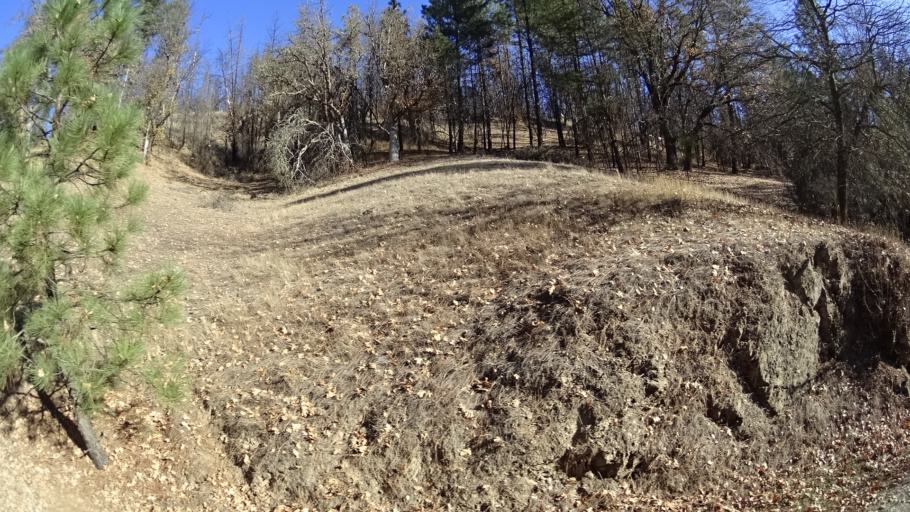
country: US
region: California
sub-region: Siskiyou County
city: Happy Camp
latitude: 41.8393
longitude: -123.0109
